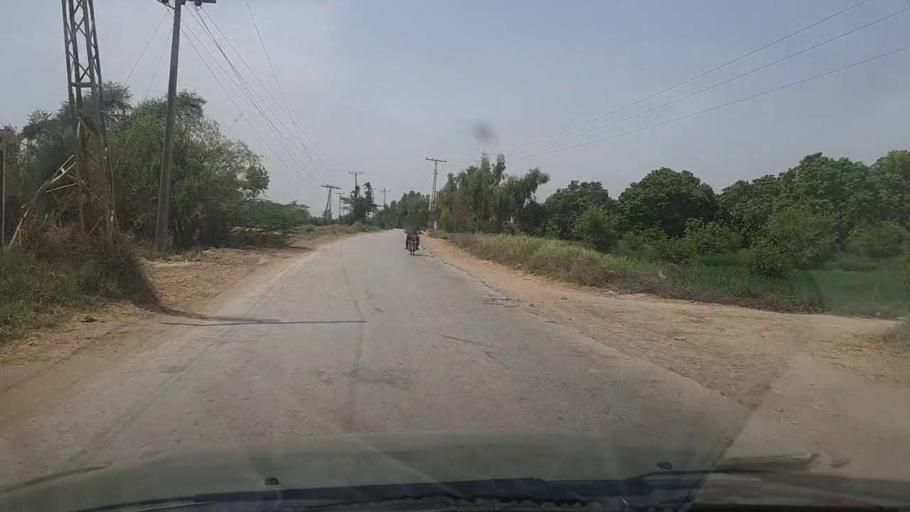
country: PK
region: Sindh
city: Bhiria
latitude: 26.9018
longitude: 68.2087
